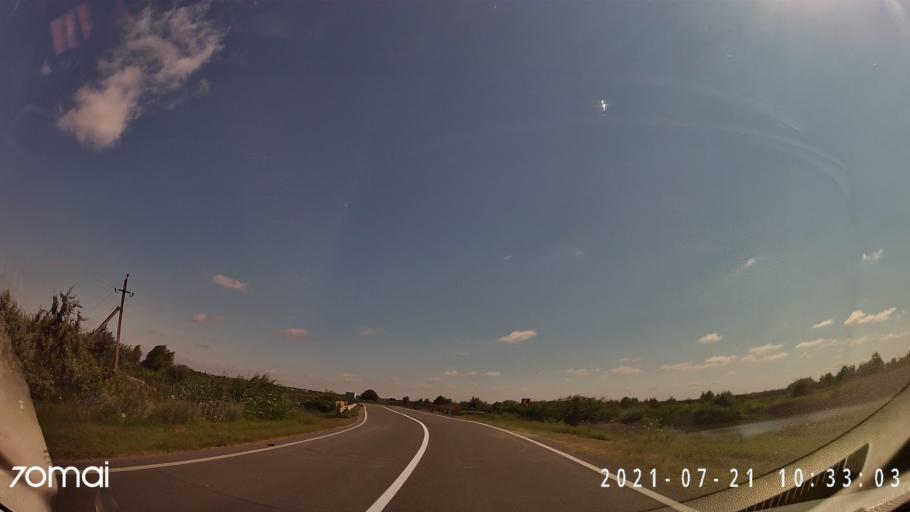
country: RO
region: Tulcea
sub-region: Oras Isaccea
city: Isaccea
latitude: 45.3015
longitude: 28.4347
